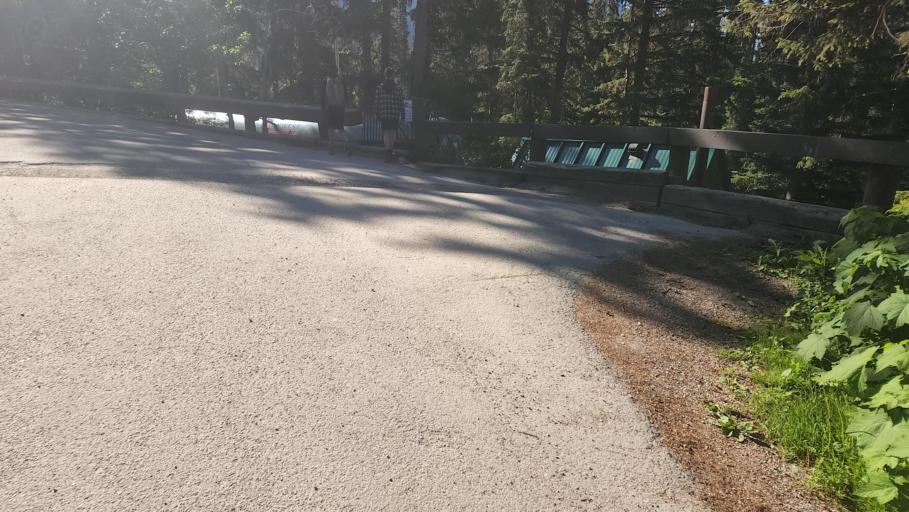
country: CA
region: Alberta
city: Lake Louise
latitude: 51.4398
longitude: -116.5390
